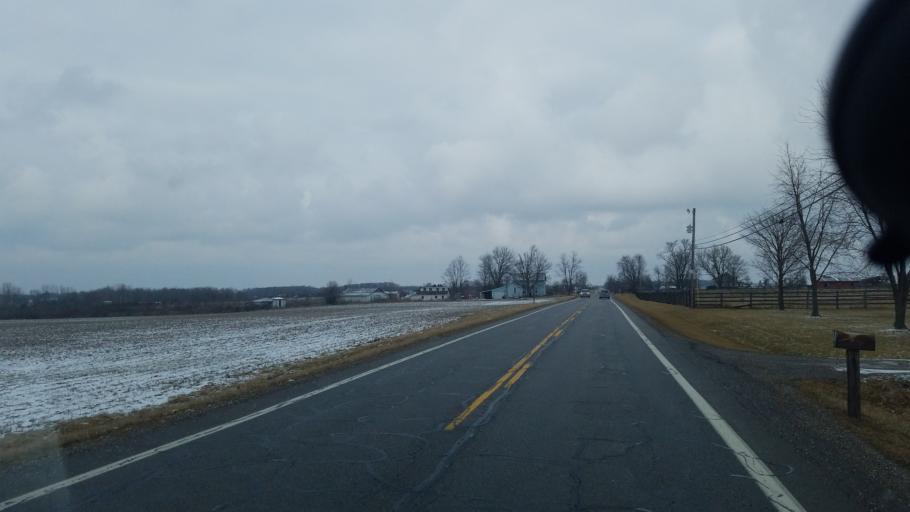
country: US
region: Ohio
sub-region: Morrow County
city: Mount Gilead
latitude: 40.6153
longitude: -82.8230
